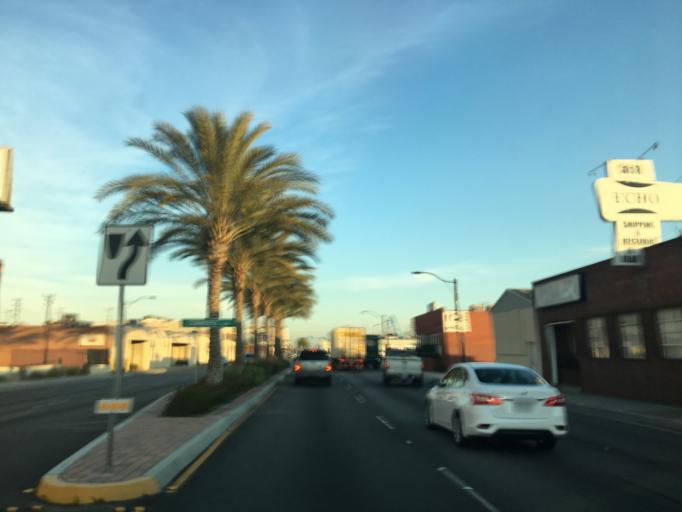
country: US
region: California
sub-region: Los Angeles County
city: Commerce
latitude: 33.9998
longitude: -118.1579
